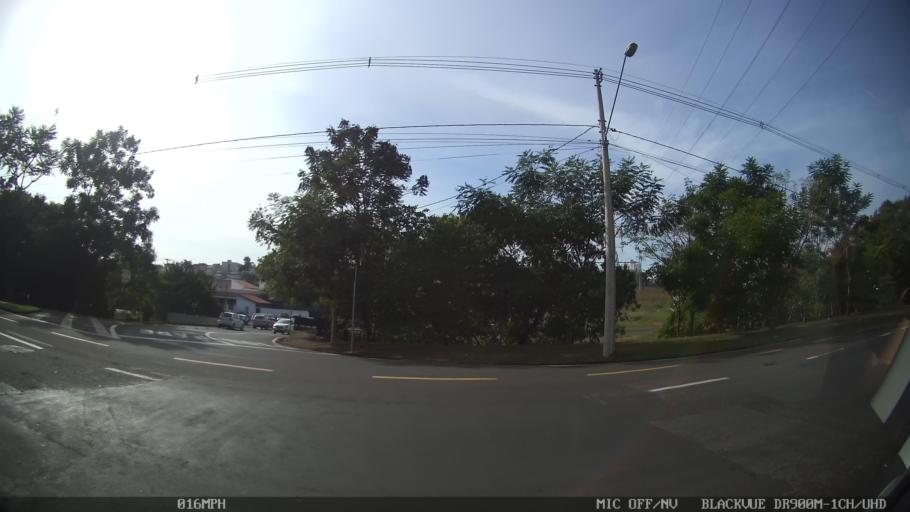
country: BR
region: Sao Paulo
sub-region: Piracicaba
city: Piracicaba
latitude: -22.7304
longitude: -47.6726
